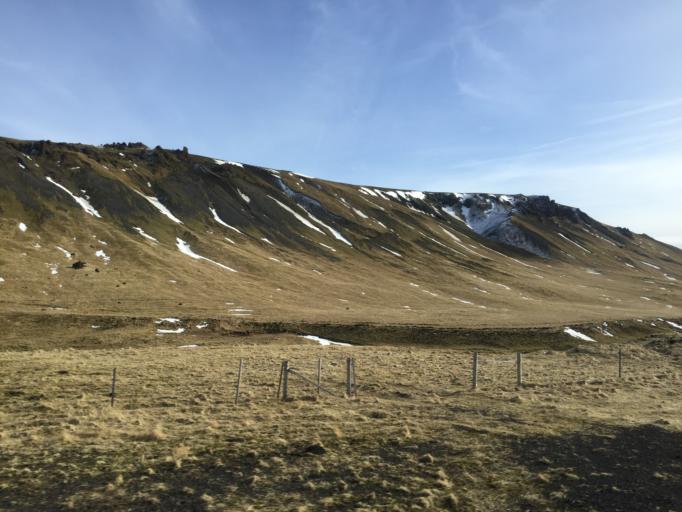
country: IS
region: South
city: Vestmannaeyjar
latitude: 63.4475
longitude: -19.0547
